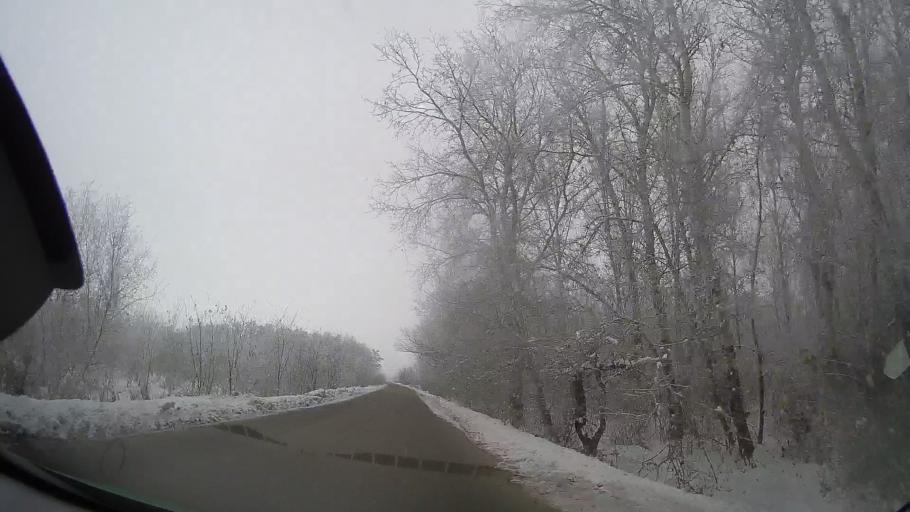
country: RO
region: Neamt
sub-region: Comuna Horia
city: Cotu Vames
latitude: 46.8866
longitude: 26.9686
